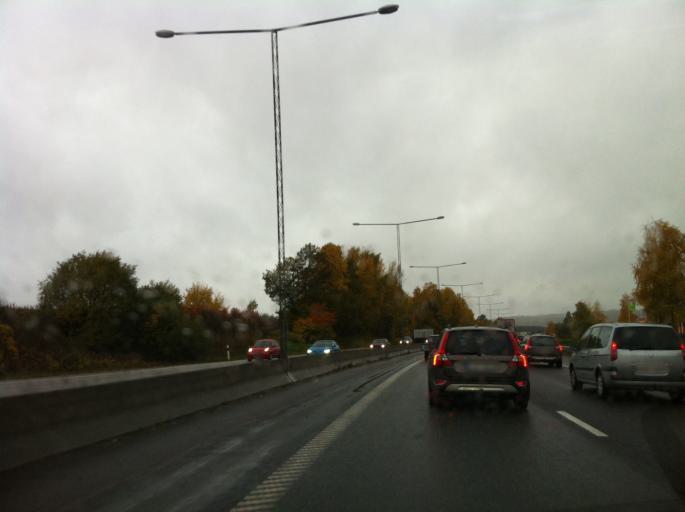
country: SE
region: Joenkoeping
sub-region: Jonkopings Kommun
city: Jonkoping
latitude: 57.7621
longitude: 14.1879
